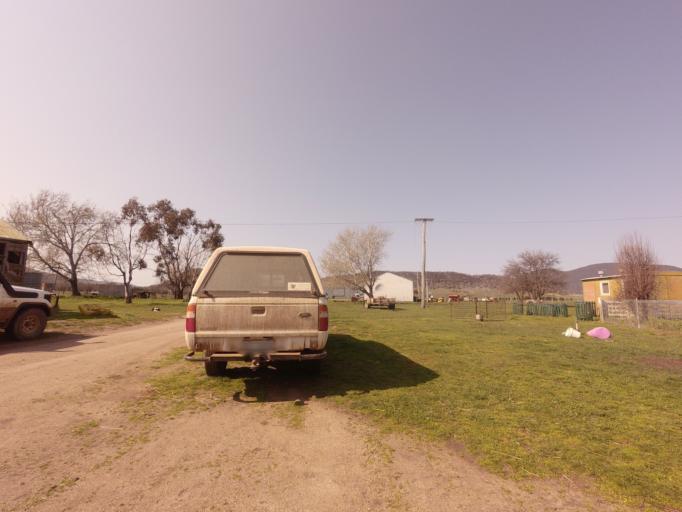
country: AU
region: Tasmania
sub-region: Break O'Day
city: St Helens
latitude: -41.8073
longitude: 147.9457
